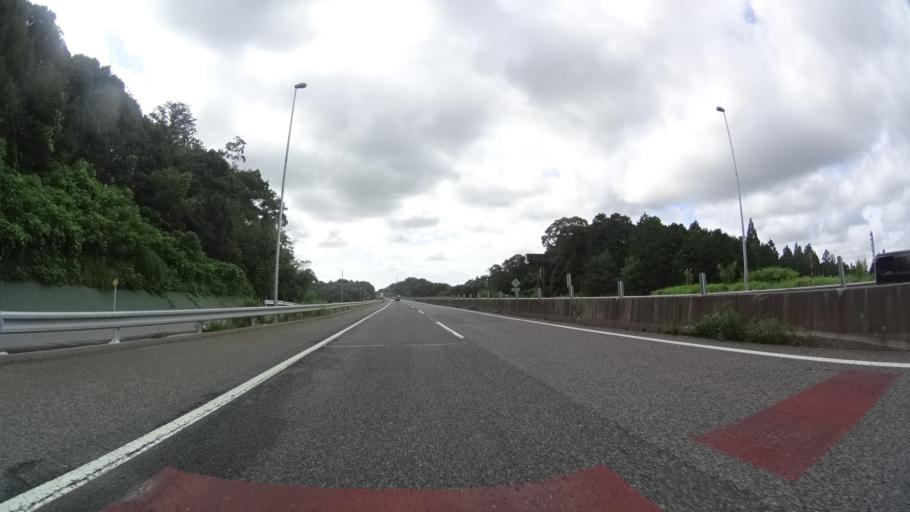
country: JP
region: Mie
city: Kameyama
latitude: 34.9045
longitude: 136.4379
